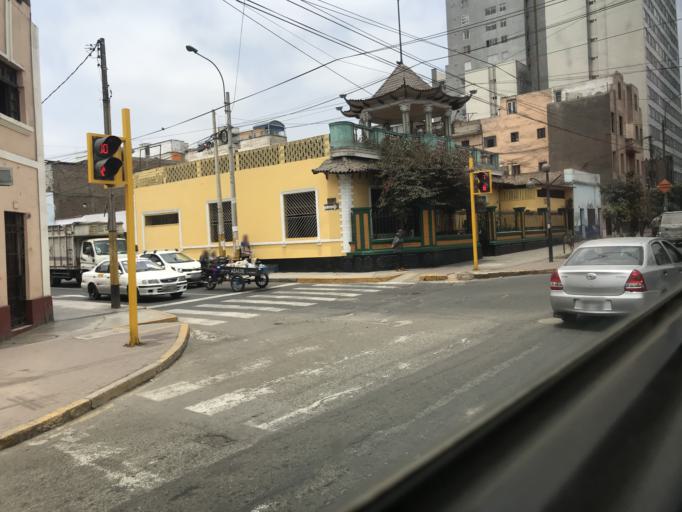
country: PE
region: Lima
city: Lima
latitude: -12.0568
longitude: -77.0481
